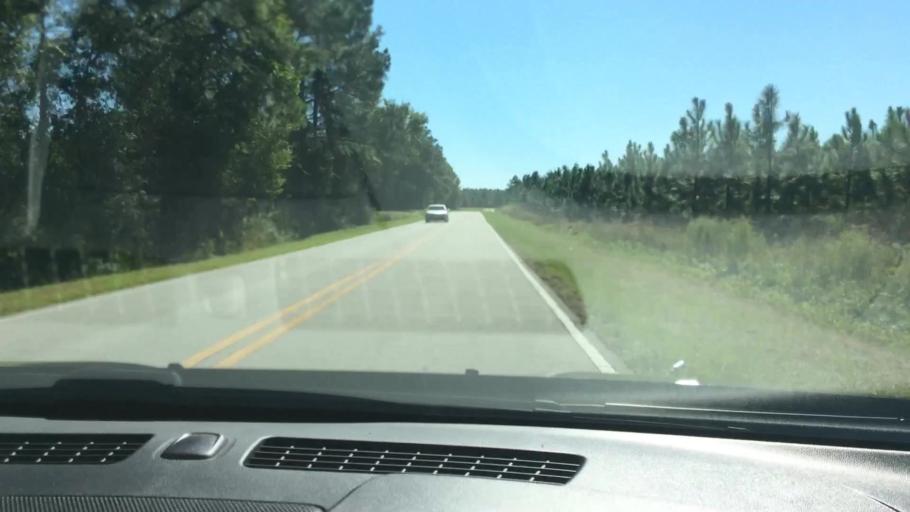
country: US
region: North Carolina
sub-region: Pitt County
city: Grifton
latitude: 35.3322
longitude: -77.3008
